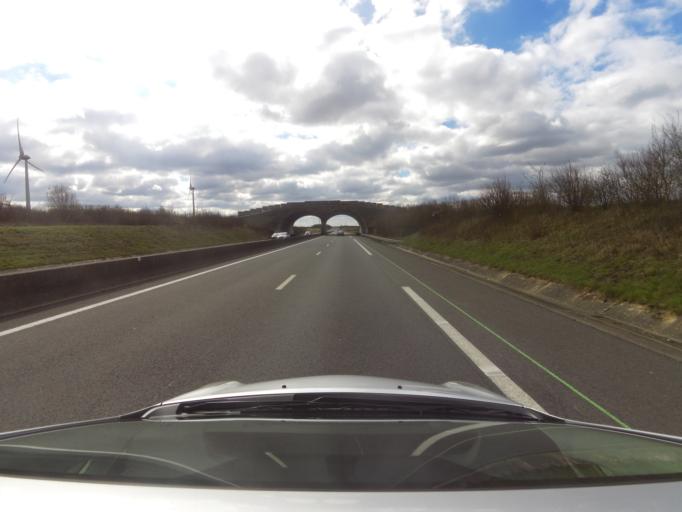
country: FR
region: Picardie
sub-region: Departement de la Somme
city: Rue
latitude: 50.3038
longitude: 1.7252
